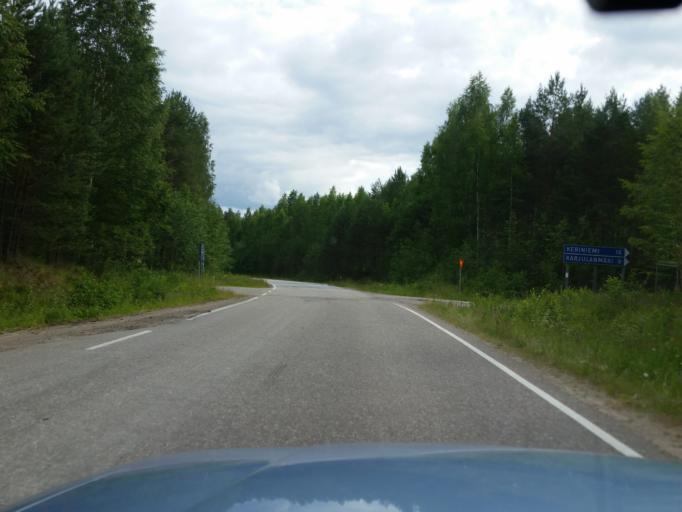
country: FI
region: Southern Savonia
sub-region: Savonlinna
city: Sulkava
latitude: 61.7424
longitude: 28.3591
